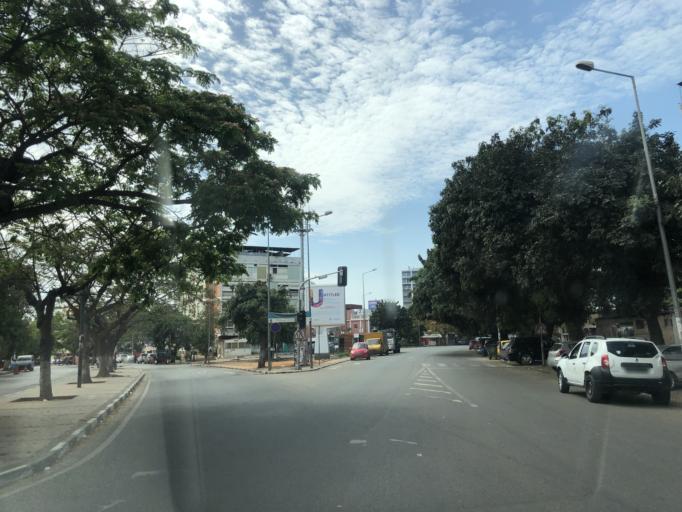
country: AO
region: Luanda
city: Luanda
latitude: -8.8253
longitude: 13.2415
